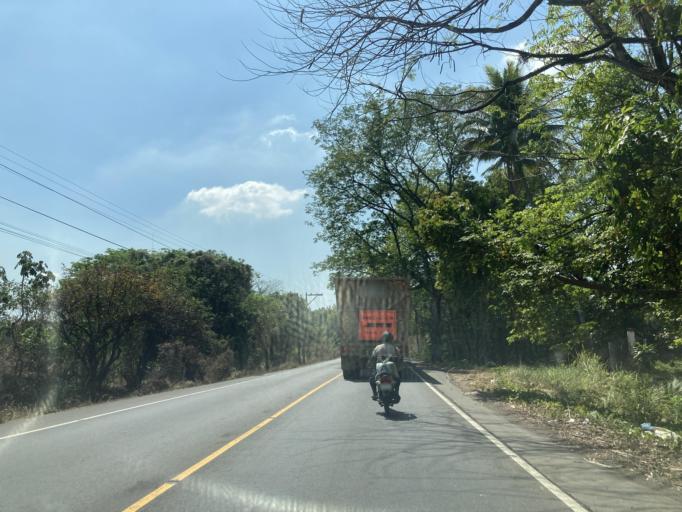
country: GT
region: Escuintla
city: Guanagazapa
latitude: 14.2139
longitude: -90.7235
